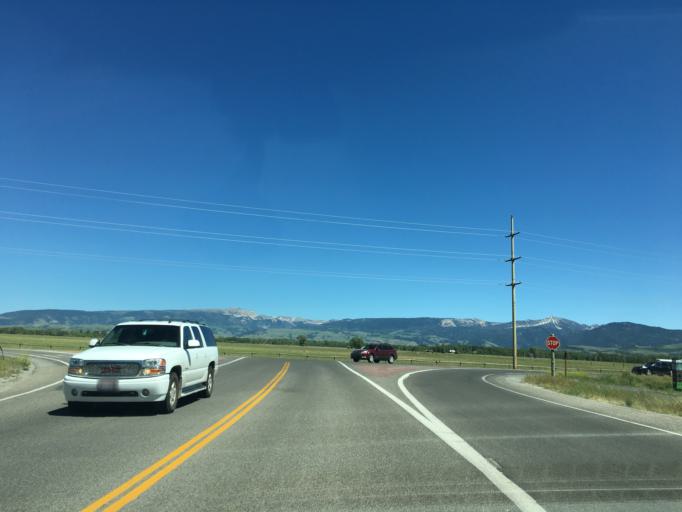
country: US
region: Wyoming
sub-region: Teton County
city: Moose Wilson Road
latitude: 43.5830
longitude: -110.8227
